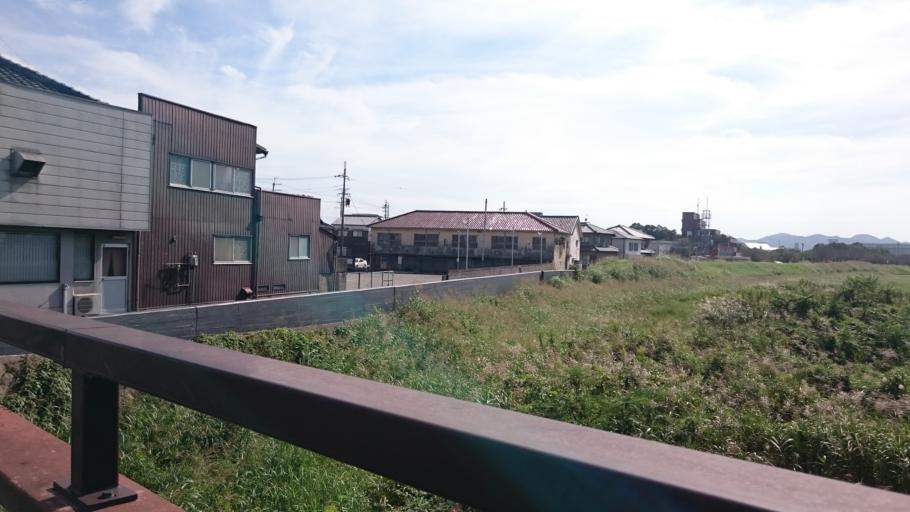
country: JP
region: Hyogo
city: Tatsunocho-tominaga
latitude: 34.8632
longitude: 134.5484
